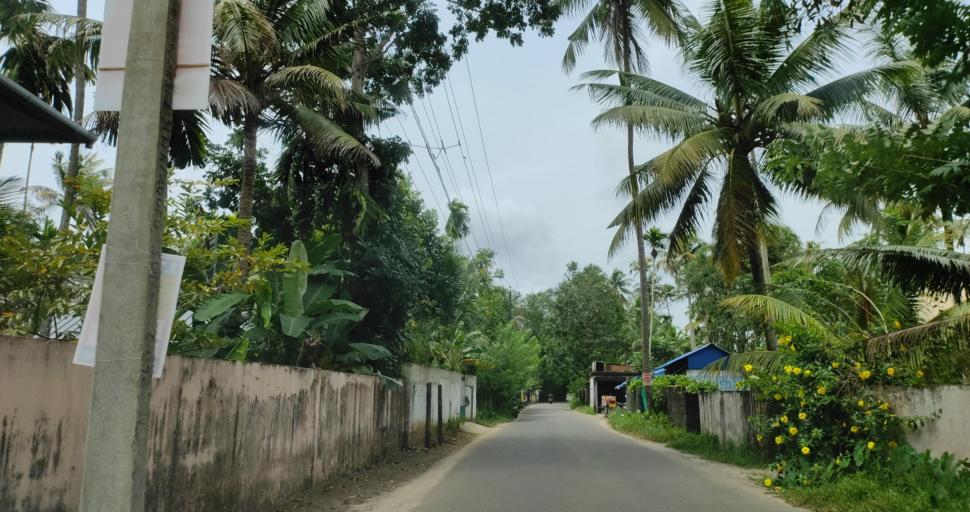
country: IN
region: Kerala
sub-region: Alappuzha
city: Shertallai
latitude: 9.6708
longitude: 76.3543
